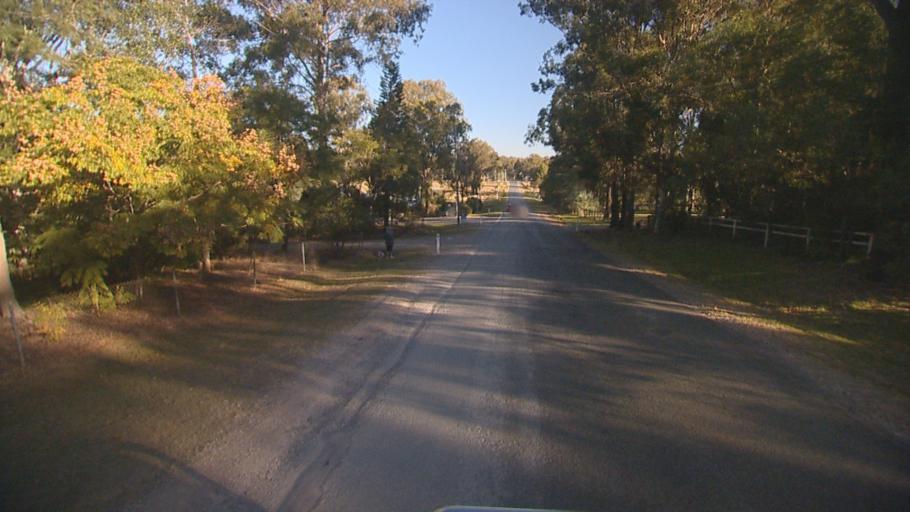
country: AU
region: Queensland
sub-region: Logan
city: Chambers Flat
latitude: -27.7795
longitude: 153.1357
